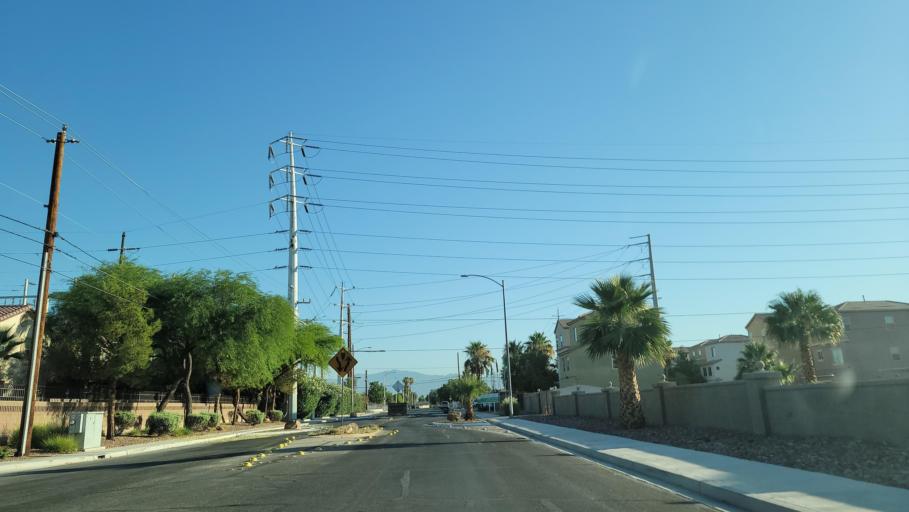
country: US
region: Nevada
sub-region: Clark County
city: Las Vegas
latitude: 36.1691
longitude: -115.1654
